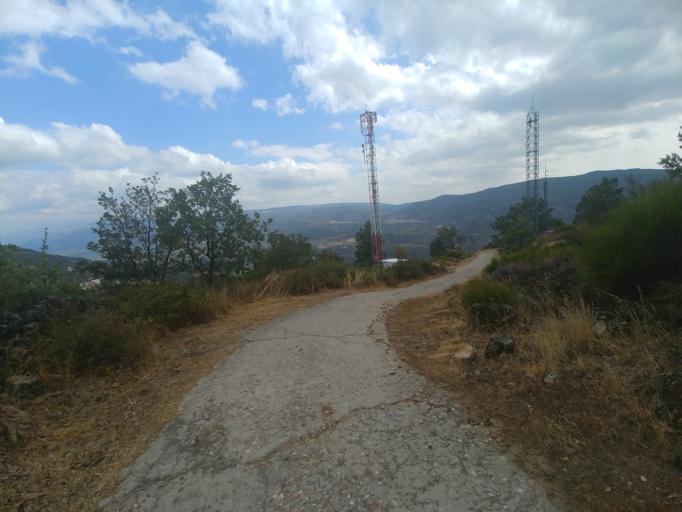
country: ES
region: Extremadura
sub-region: Provincia de Caceres
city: Cabezabellosa
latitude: 40.1331
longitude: -5.9518
